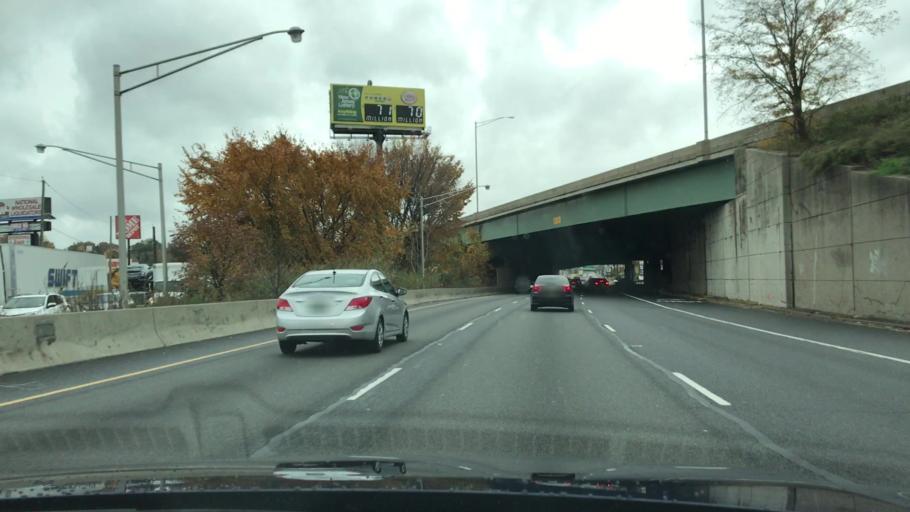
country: US
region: New Jersey
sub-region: Bergen County
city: Lodi
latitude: 40.8870
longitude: -74.0687
